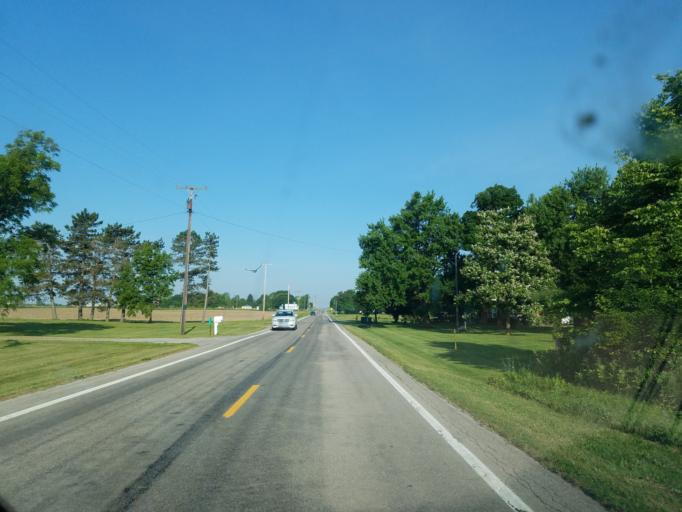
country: US
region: Ohio
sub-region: Hardin County
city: Kenton
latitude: 40.7318
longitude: -83.6383
